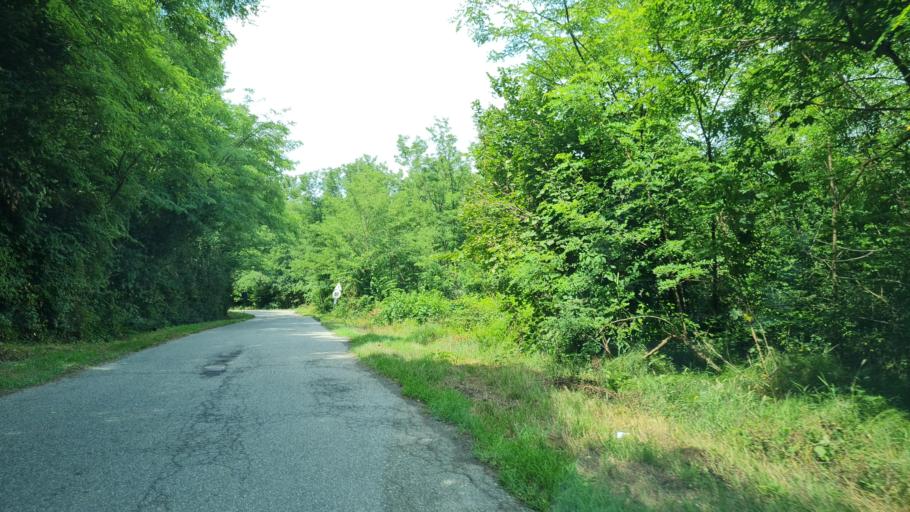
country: IT
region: Piedmont
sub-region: Provincia di Biella
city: Masserano
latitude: 45.5622
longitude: 8.2300
